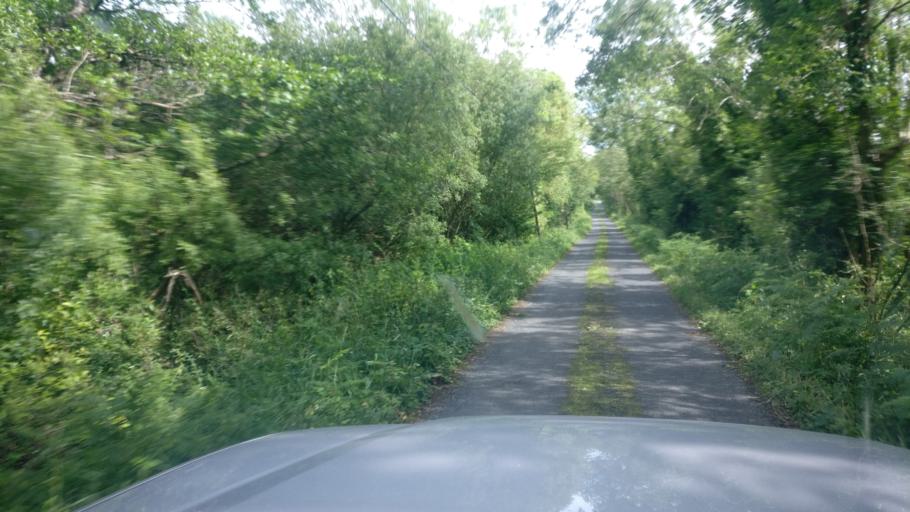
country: IE
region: Connaught
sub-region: County Galway
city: Gort
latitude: 53.0745
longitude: -8.7719
